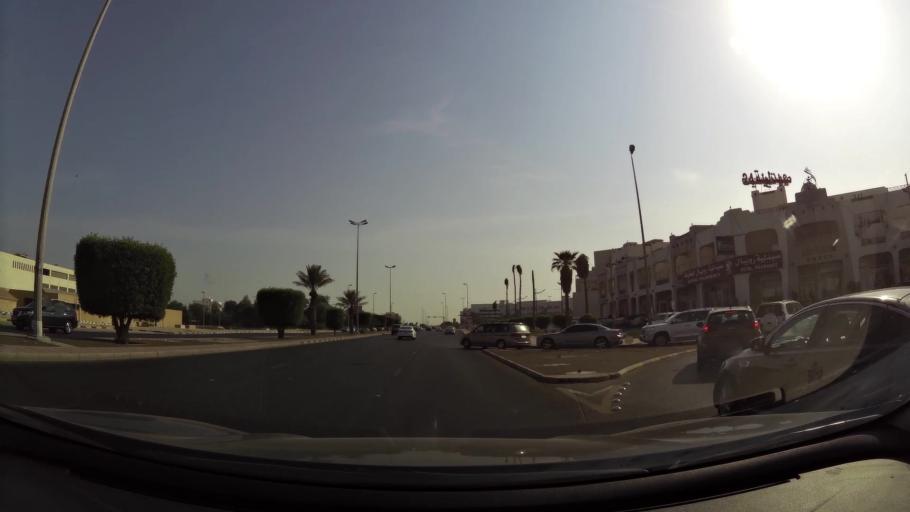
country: KW
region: Al Ahmadi
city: Al Fintas
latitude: 29.1707
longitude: 48.1004
